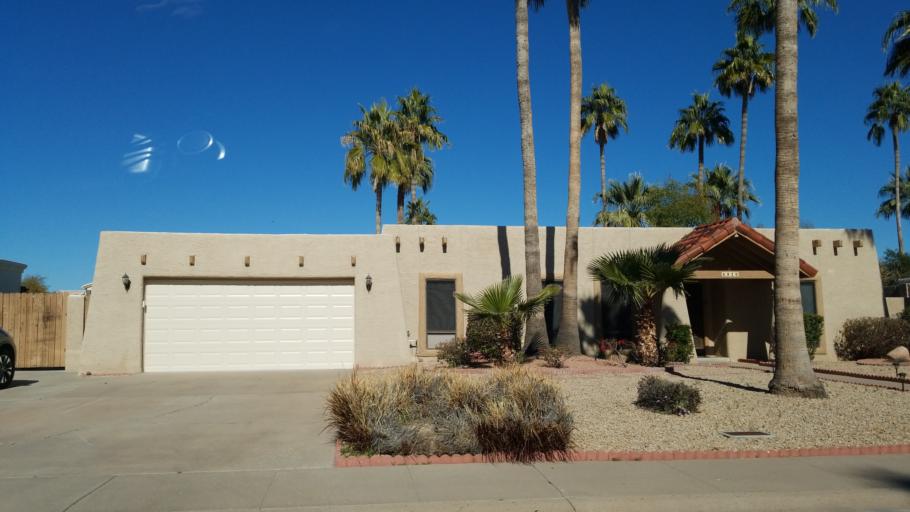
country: US
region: Arizona
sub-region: Maricopa County
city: Paradise Valley
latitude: 33.6142
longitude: -111.9314
